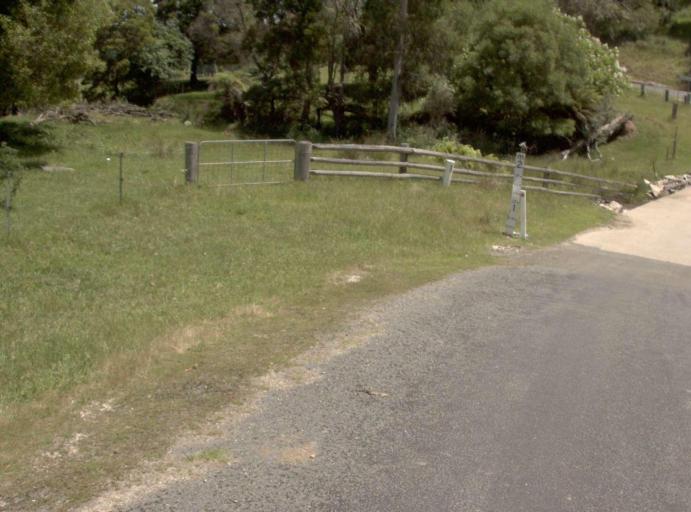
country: AU
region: New South Wales
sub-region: Bombala
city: Bombala
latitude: -37.3589
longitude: 149.0238
